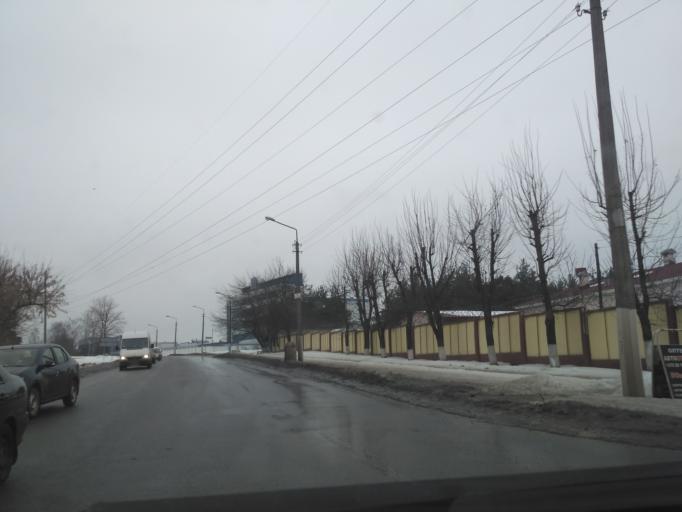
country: BY
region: Minsk
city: Horad Barysaw
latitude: 54.1978
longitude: 28.5142
